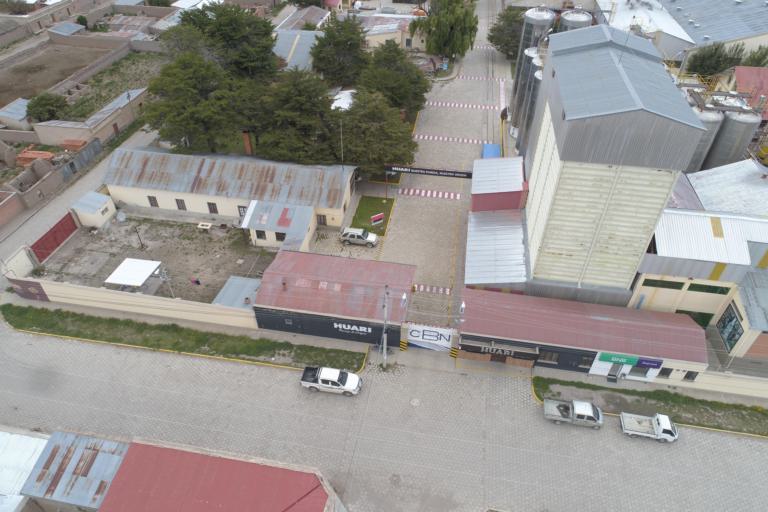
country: BO
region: Oruro
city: Challapata
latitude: -19.0118
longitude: -66.7795
